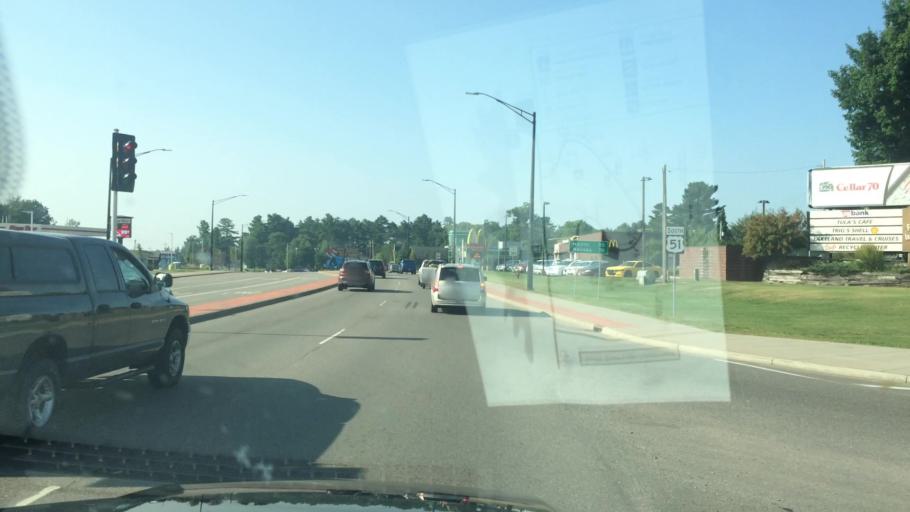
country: US
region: Wisconsin
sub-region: Vilas County
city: Lac du Flambeau
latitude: 45.8874
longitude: -89.7041
